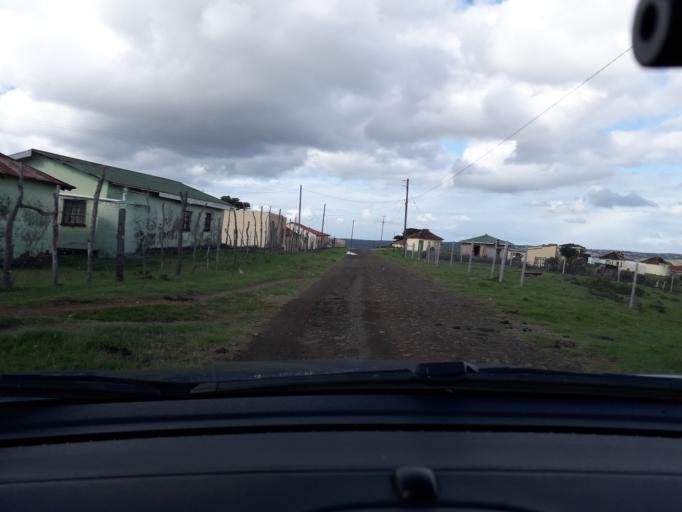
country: ZA
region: Eastern Cape
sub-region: Buffalo City Metropolitan Municipality
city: Bhisho
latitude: -33.1146
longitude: 27.4292
